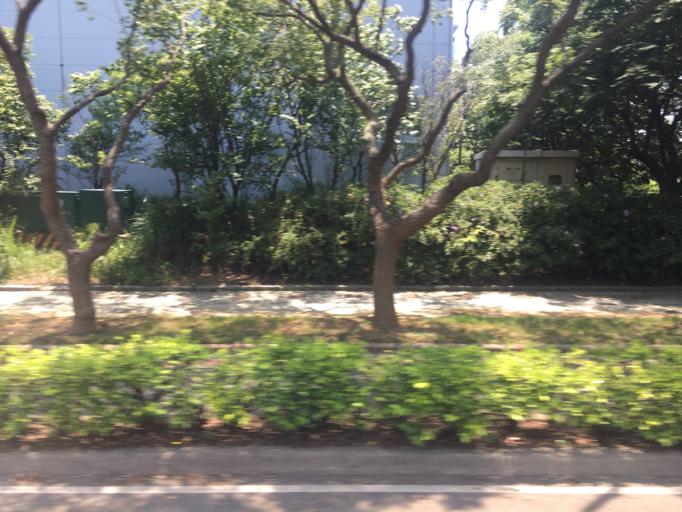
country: TW
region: Taiwan
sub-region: Hsinchu
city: Hsinchu
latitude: 24.7766
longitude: 121.0096
